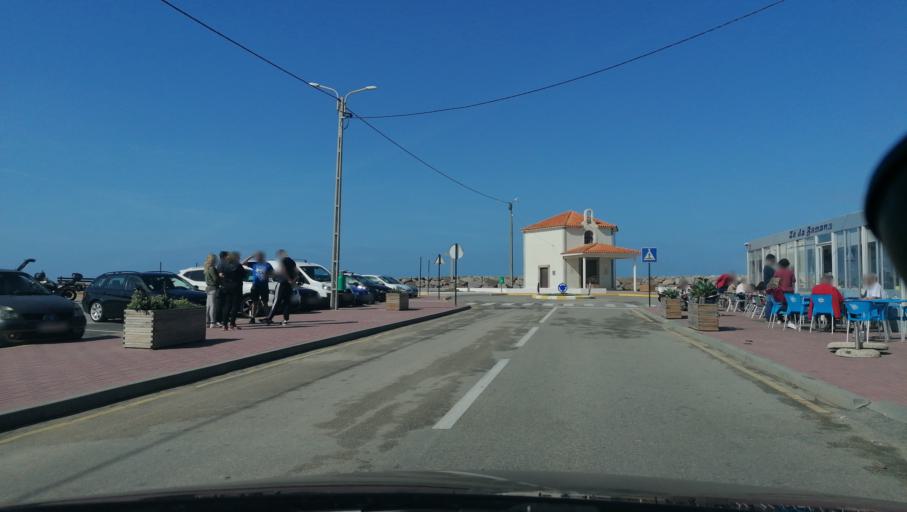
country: PT
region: Aveiro
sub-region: Espinho
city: Silvalde
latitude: 40.9781
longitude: -8.6487
